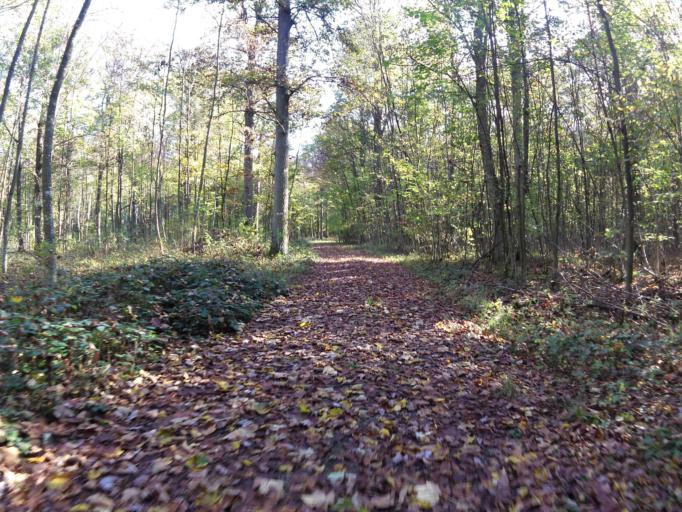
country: DE
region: Bavaria
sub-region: Regierungsbezirk Unterfranken
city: Sulzfeld am Main
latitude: 49.7191
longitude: 10.0945
